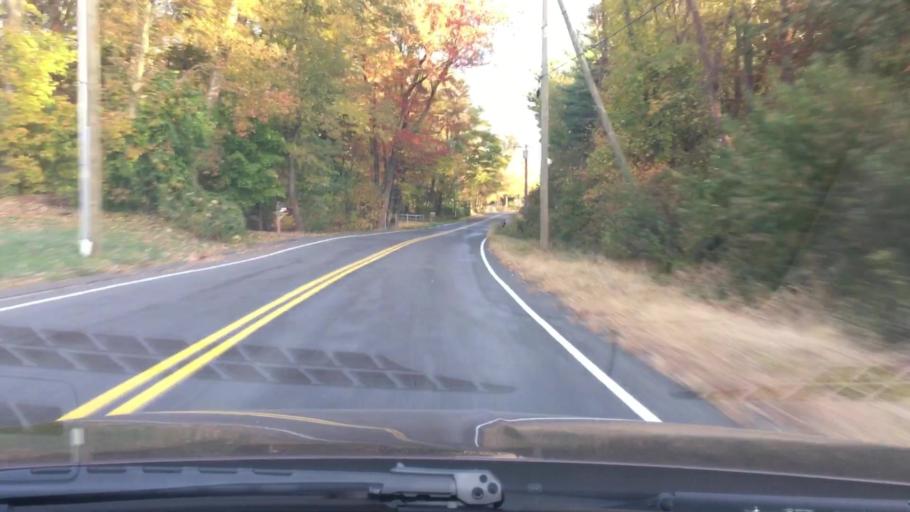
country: US
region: Connecticut
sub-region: Tolland County
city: Somers
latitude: 42.0082
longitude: -72.4809
